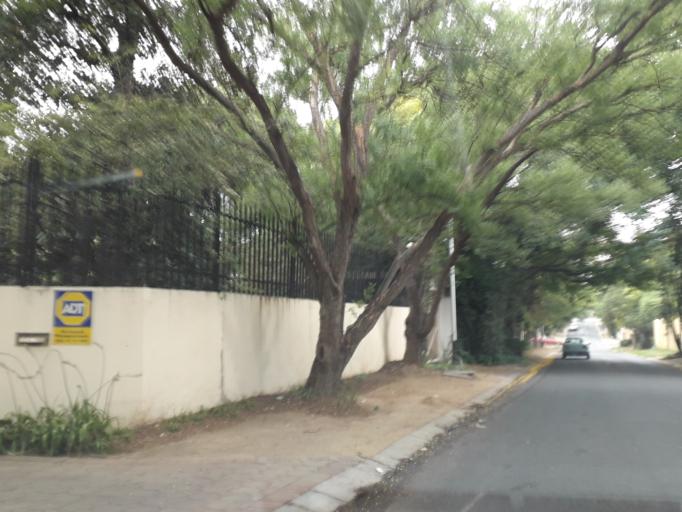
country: ZA
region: Gauteng
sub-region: City of Johannesburg Metropolitan Municipality
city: Roodepoort
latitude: -26.1030
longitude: 27.9682
